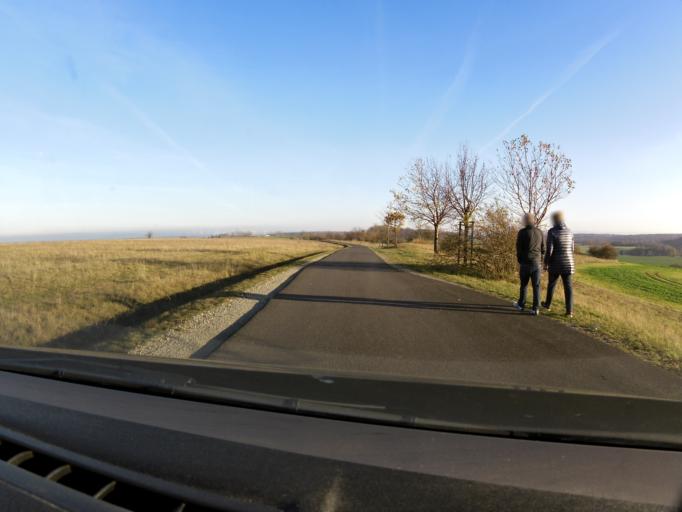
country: DE
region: Thuringia
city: Weberstedt
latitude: 51.0671
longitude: 10.4673
